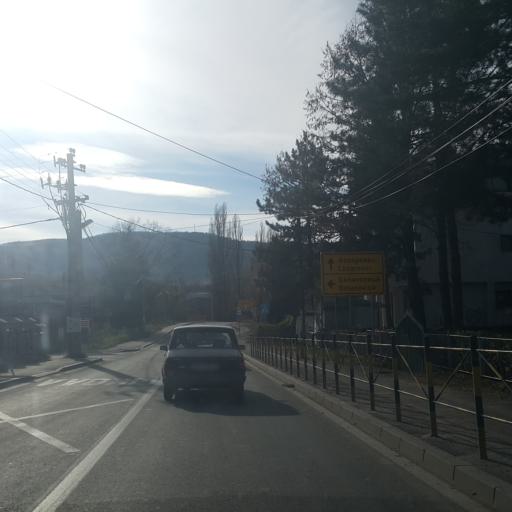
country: RS
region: Central Serbia
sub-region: Sumadijski Okrug
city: Arangelovac
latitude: 44.3361
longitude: 20.4567
